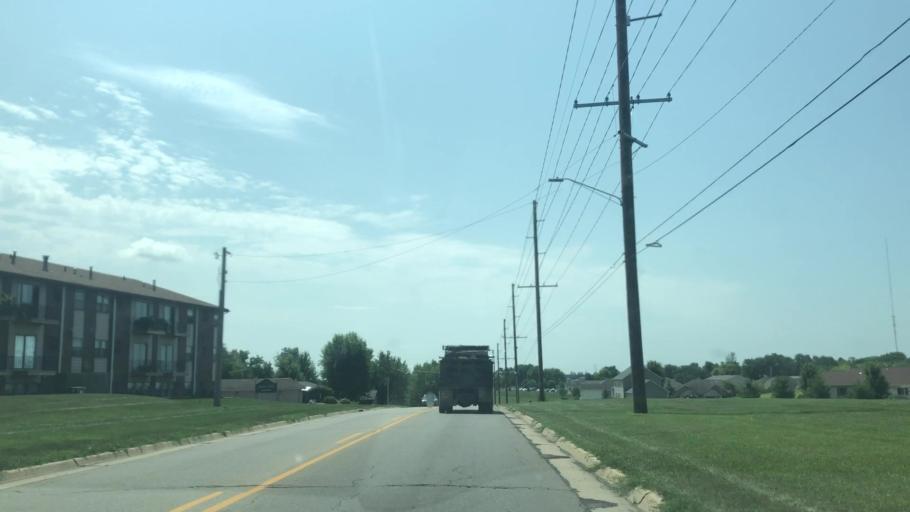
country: US
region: Iowa
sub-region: Marshall County
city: Marshalltown
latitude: 42.0164
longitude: -92.9222
